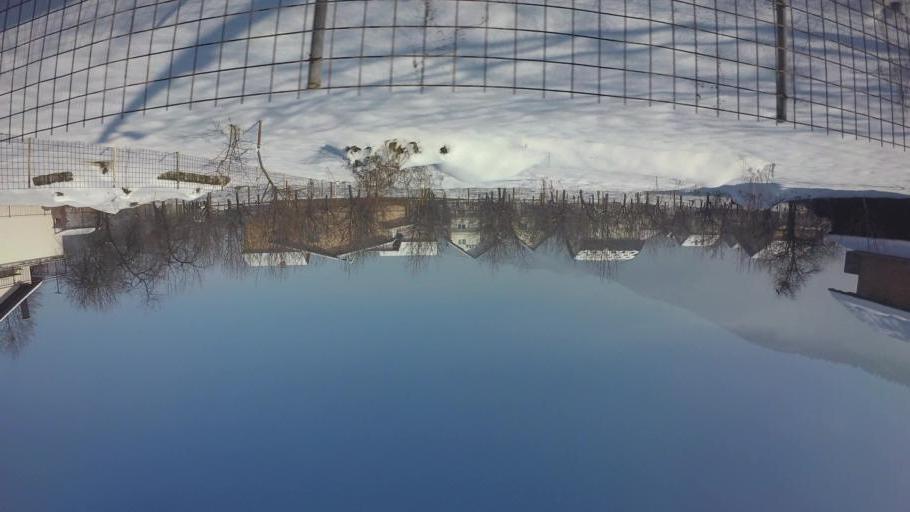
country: BA
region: Federation of Bosnia and Herzegovina
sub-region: Kanton Sarajevo
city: Sarajevo
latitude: 43.8018
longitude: 18.3075
